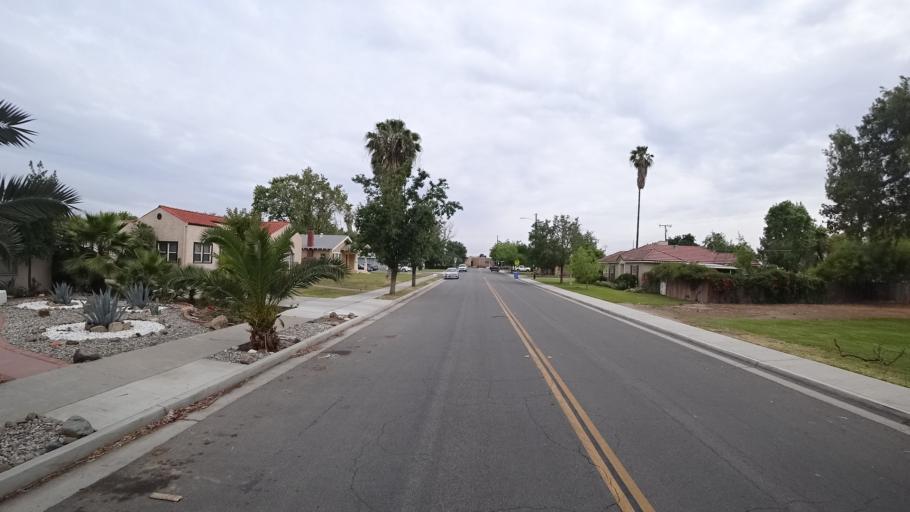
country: US
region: California
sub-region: Kings County
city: Hanford
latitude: 36.3412
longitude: -119.6444
